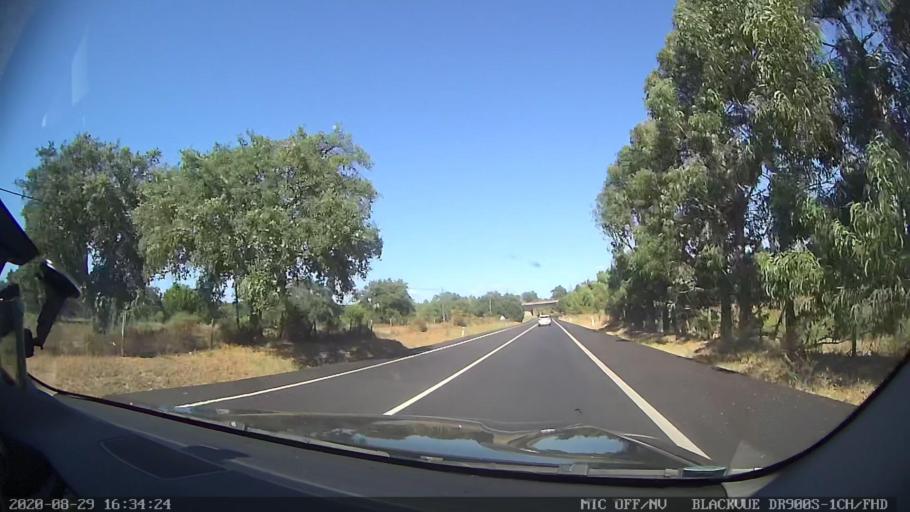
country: PT
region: Setubal
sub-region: Setubal
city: Setubal
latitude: 38.5775
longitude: -8.7425
